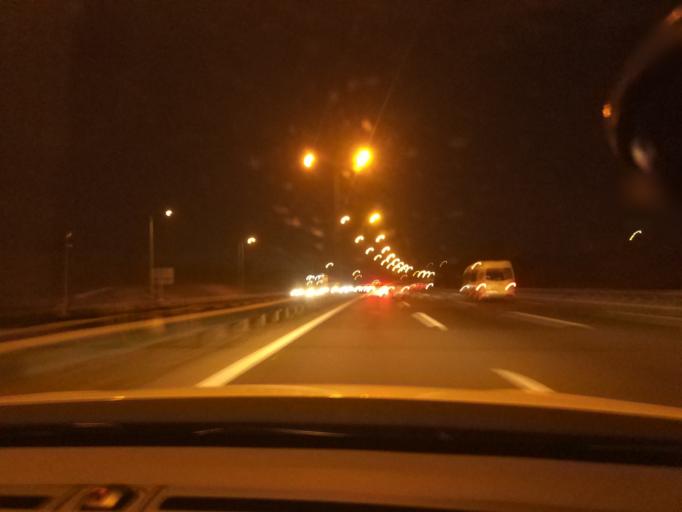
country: TR
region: Istanbul
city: Umraniye
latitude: 41.0583
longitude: 29.1178
